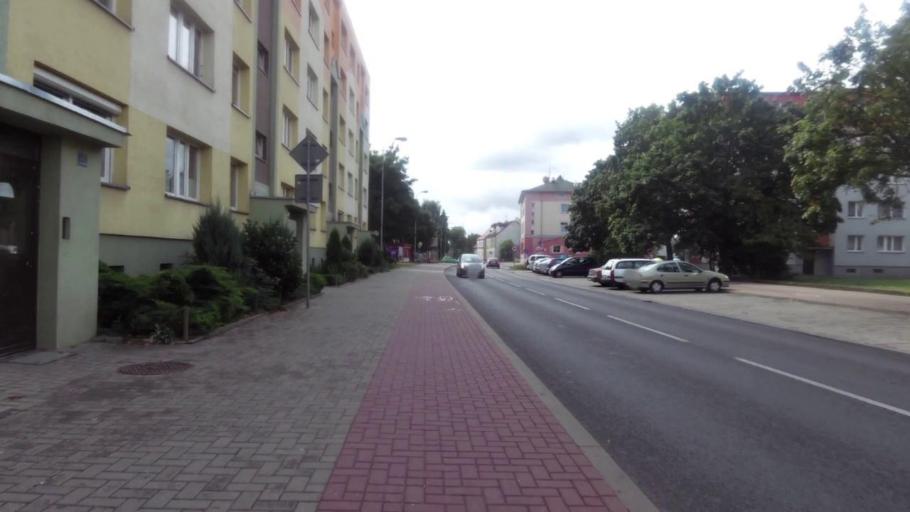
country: PL
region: West Pomeranian Voivodeship
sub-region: Powiat mysliborski
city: Debno
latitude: 52.7360
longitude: 14.6961
